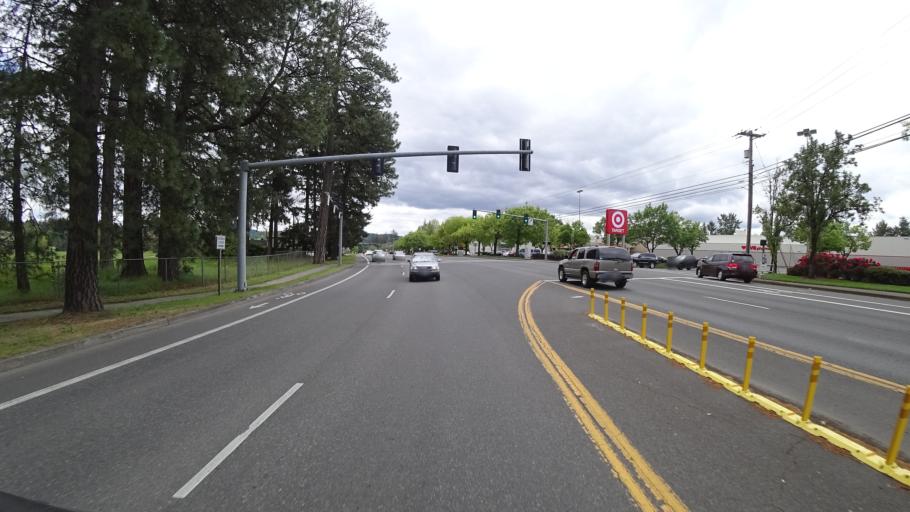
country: US
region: Oregon
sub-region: Washington County
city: Metzger
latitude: 45.4549
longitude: -122.7787
